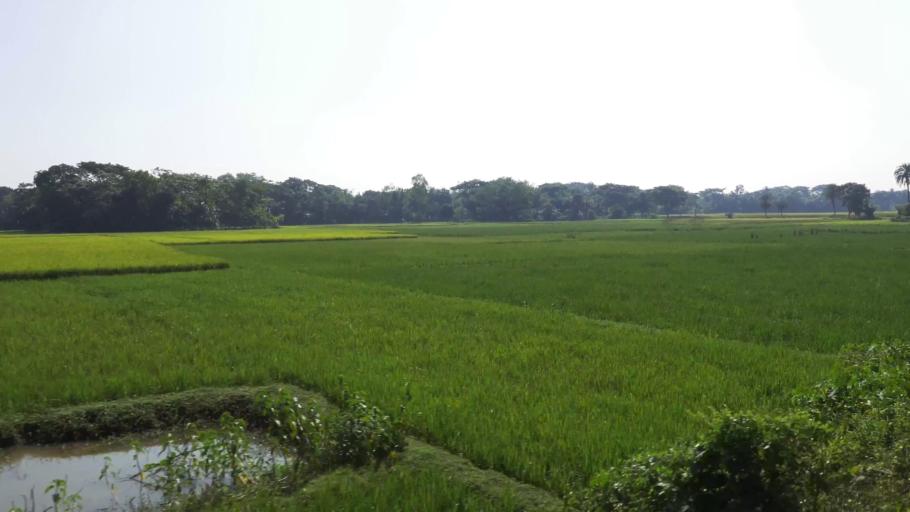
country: BD
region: Dhaka
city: Gafargaon
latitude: 24.5791
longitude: 90.5080
